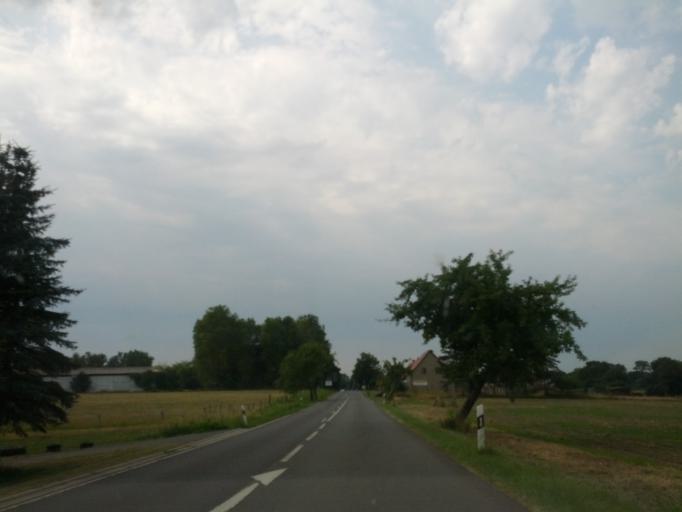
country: DE
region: Brandenburg
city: Kremmen
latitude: 52.7545
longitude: 12.8931
